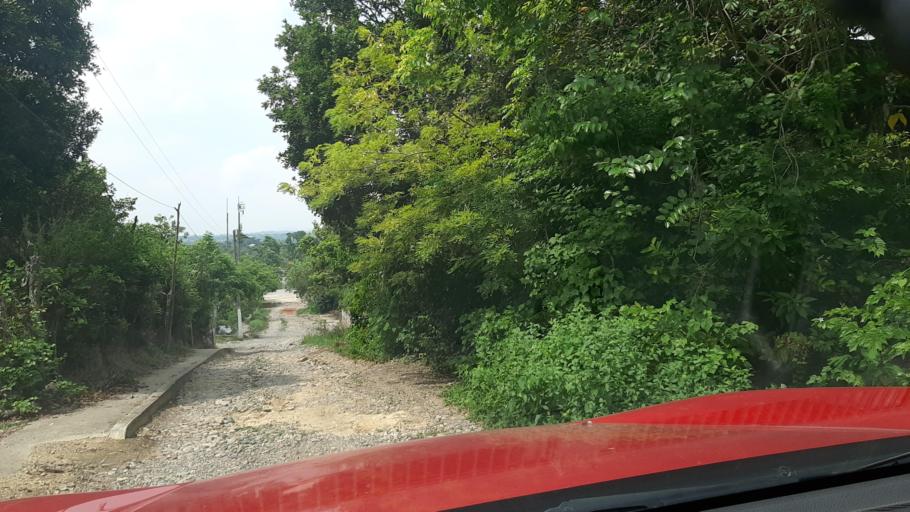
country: MX
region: Veracruz
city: Gutierrez Zamora
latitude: 20.4476
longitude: -97.1652
